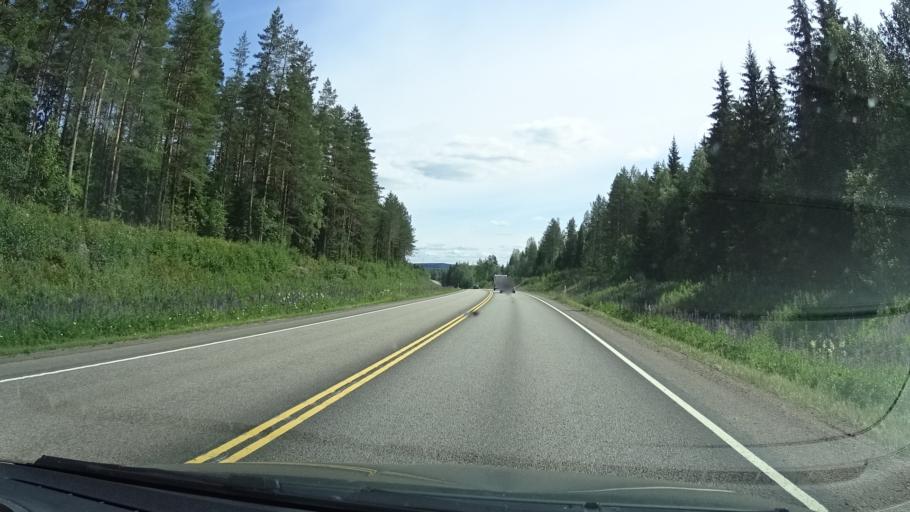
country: FI
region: Central Finland
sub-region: Jyvaeskylae
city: Petaejaevesi
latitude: 62.2672
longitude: 25.4316
